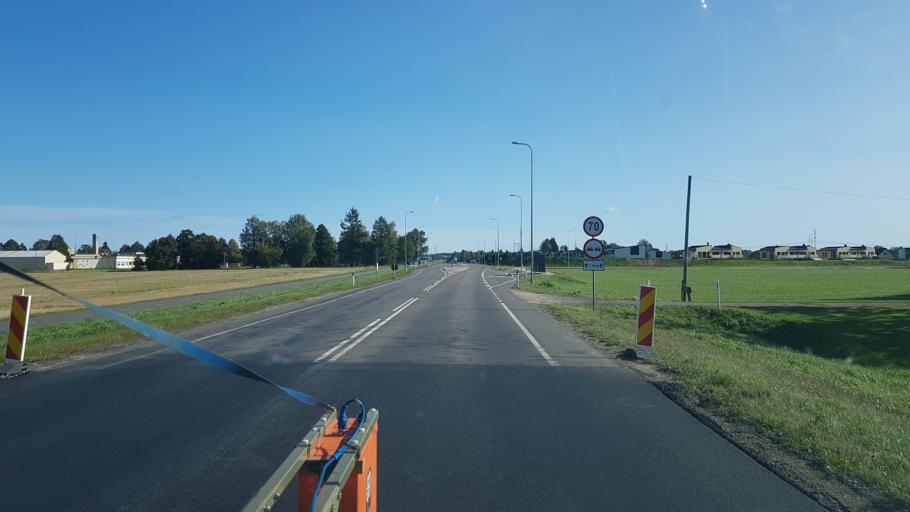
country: EE
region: Tartu
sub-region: Tartu linn
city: Tartu
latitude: 58.3589
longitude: 26.6377
